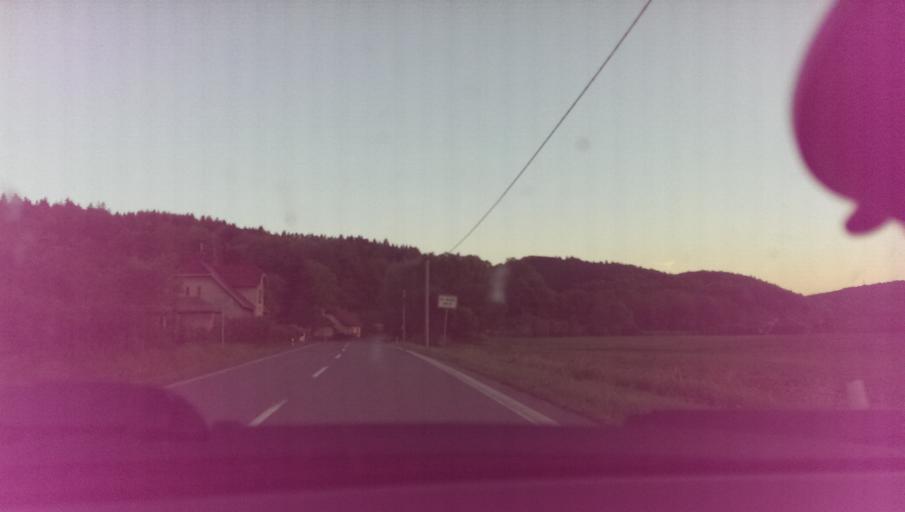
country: CZ
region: Zlin
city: Valasske Mezirici
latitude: 49.4417
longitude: 17.9708
